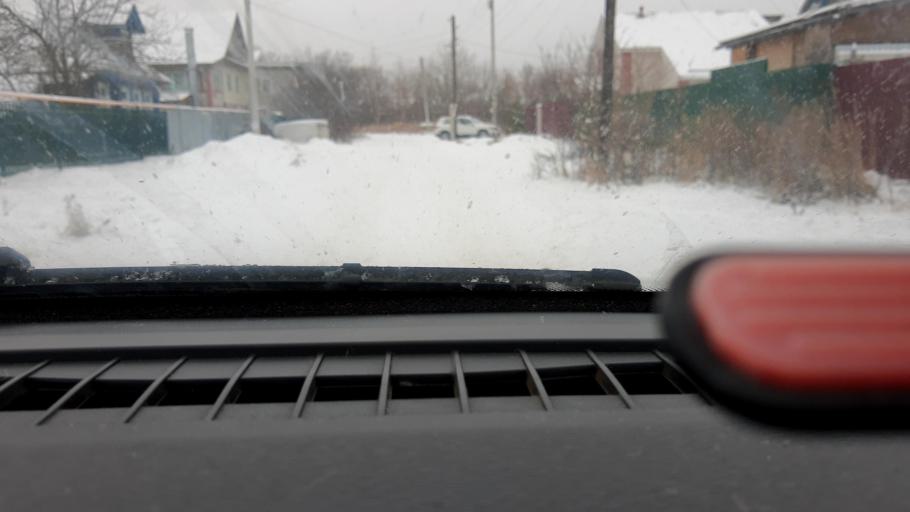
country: RU
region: Nizjnij Novgorod
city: Novaya Balakhna
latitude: 56.5174
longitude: 43.5731
